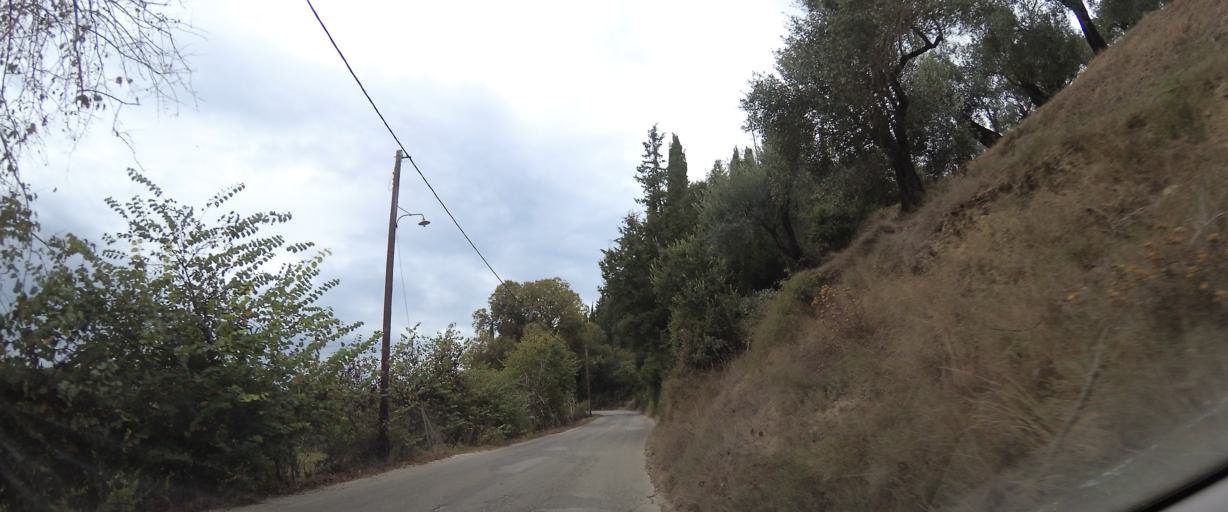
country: GR
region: Ionian Islands
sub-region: Nomos Kerkyras
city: Agios Georgis
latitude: 39.7497
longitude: 19.6849
